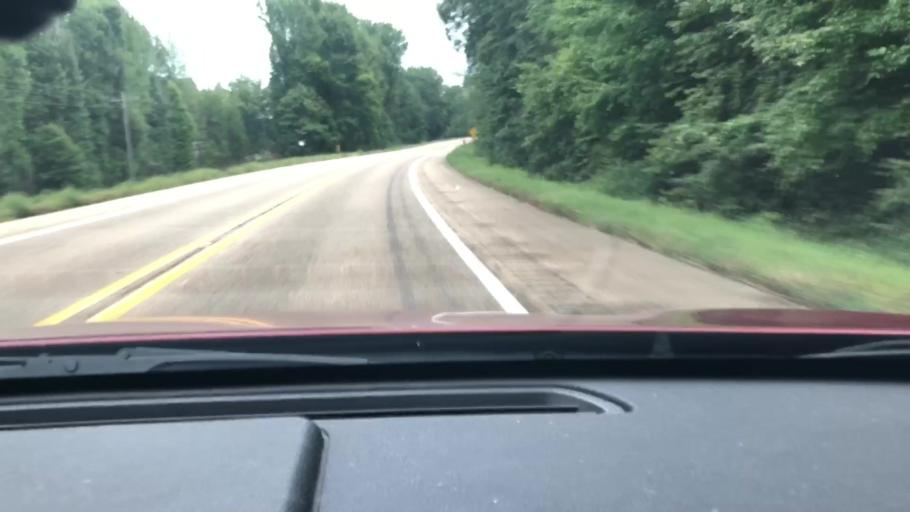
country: US
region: Arkansas
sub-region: Miller County
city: Texarkana
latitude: 33.4197
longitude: -93.8270
